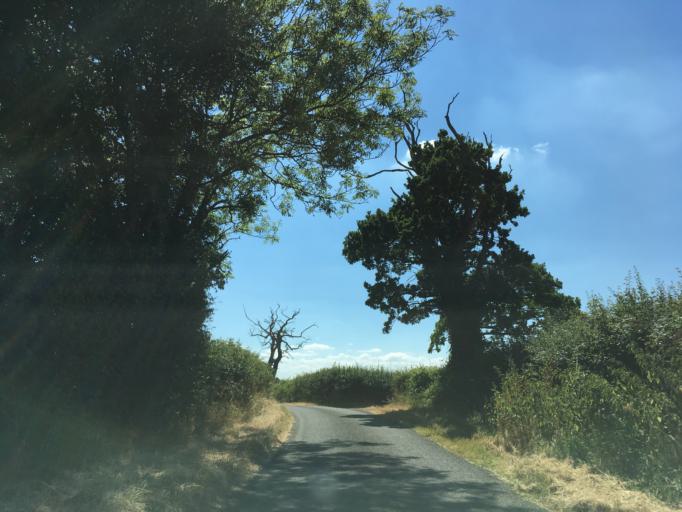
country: GB
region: England
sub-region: Wiltshire
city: Luckington
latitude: 51.5543
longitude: -2.2235
